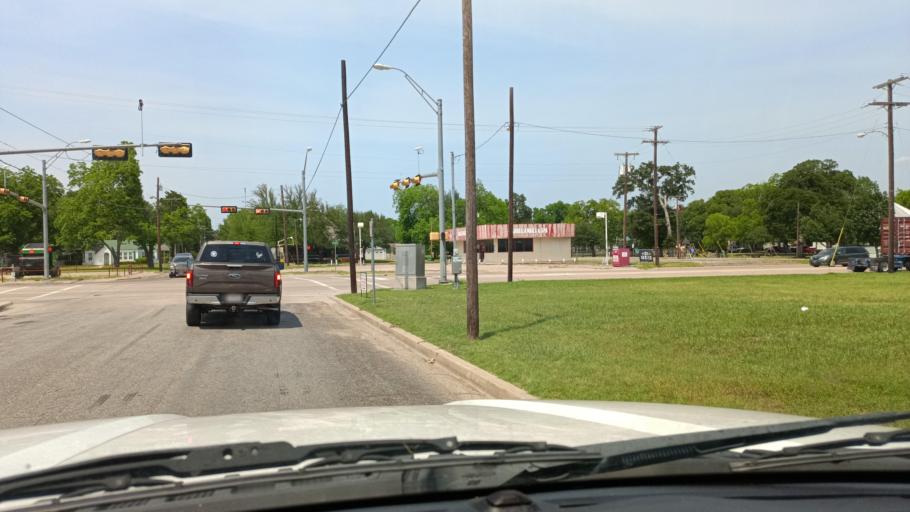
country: US
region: Texas
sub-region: Milam County
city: Cameron
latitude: 30.8522
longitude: -96.9749
